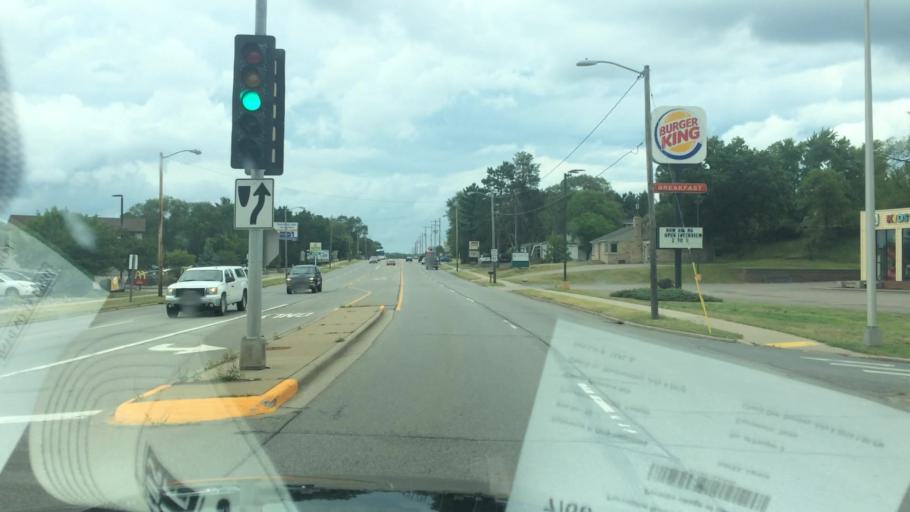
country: US
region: Wisconsin
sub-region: Marathon County
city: Schofield
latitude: 44.9018
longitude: -89.6079
